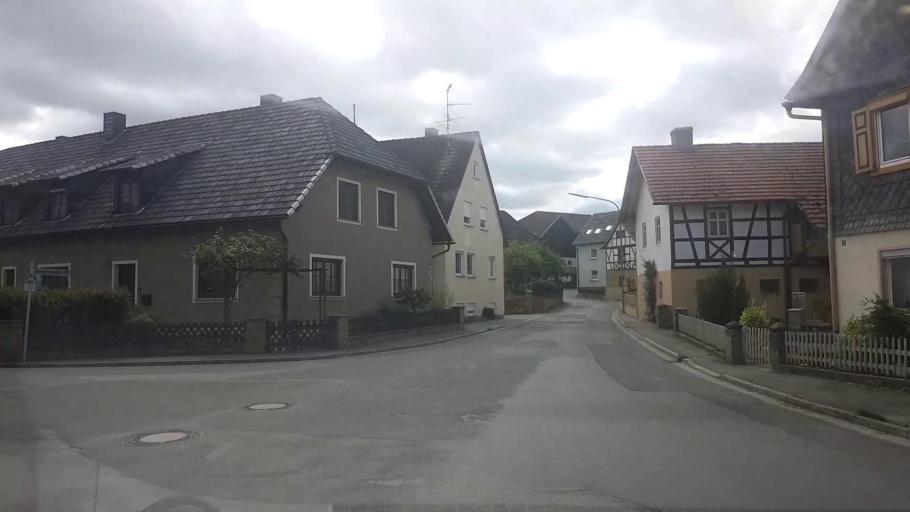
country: DE
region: Bavaria
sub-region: Upper Franconia
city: Bad Staffelstein
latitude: 50.1154
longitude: 11.0314
